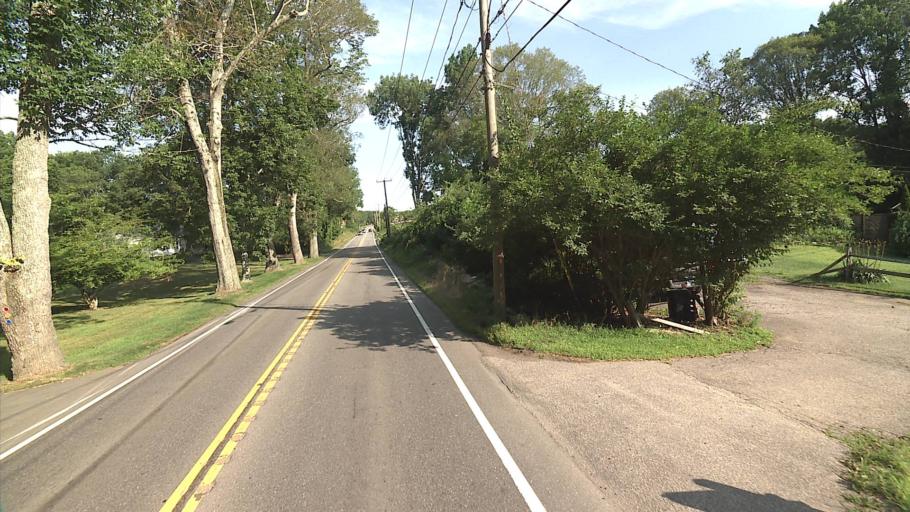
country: US
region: Connecticut
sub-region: New London County
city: Pawcatuck
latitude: 41.4308
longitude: -71.8652
